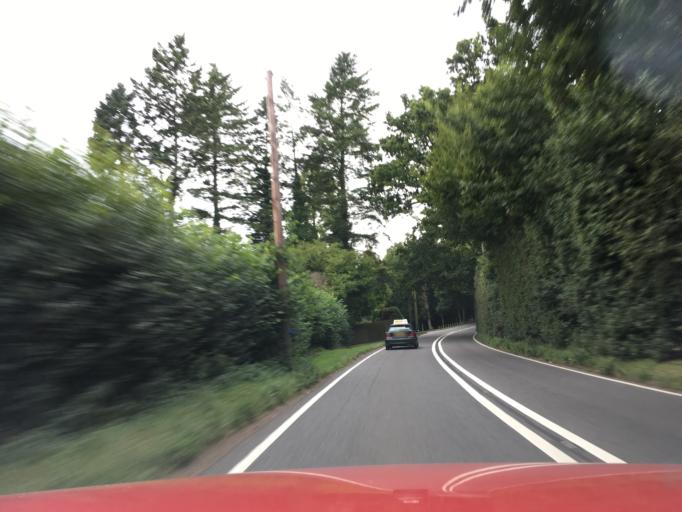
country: GB
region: England
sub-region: Hampshire
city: Petersfield
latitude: 51.0119
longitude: -0.9069
